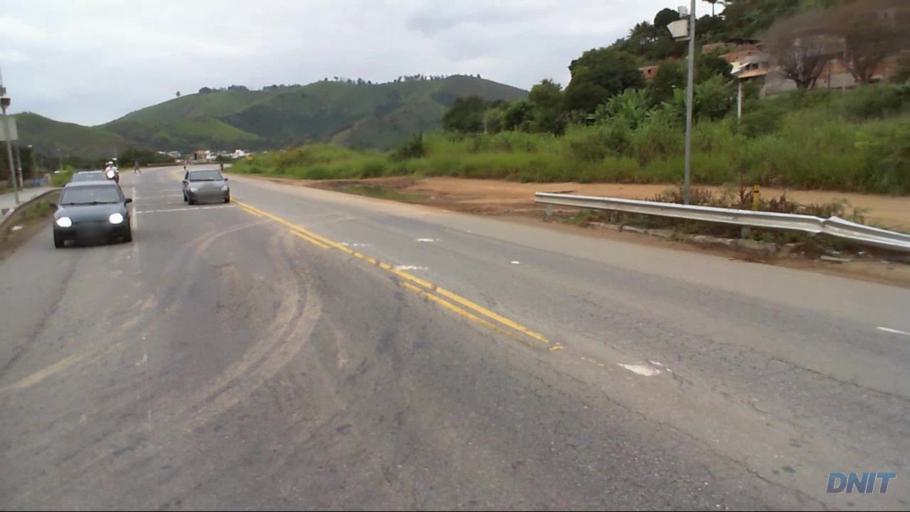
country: BR
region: Minas Gerais
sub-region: Coronel Fabriciano
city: Coronel Fabriciano
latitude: -19.5301
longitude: -42.6191
